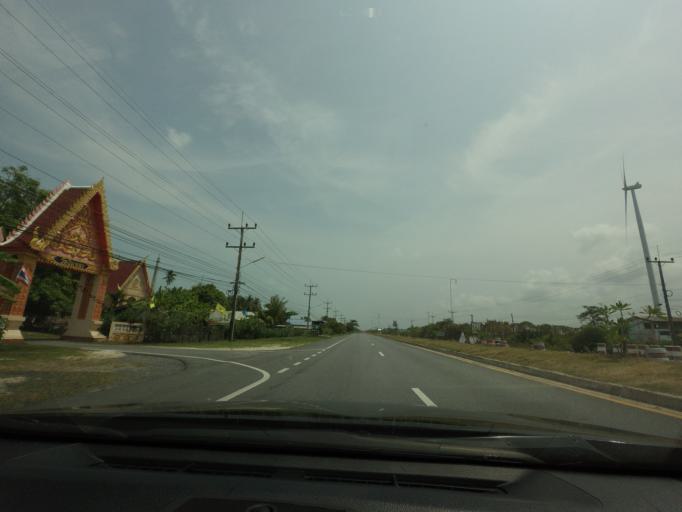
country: TH
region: Nakhon Si Thammarat
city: Hua Sai
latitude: 7.9885
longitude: 100.3246
